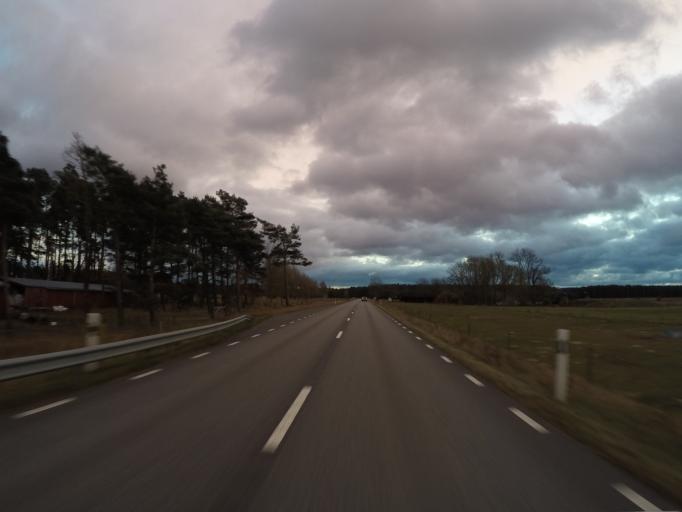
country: SE
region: Skane
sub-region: Kristianstads Kommun
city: Degeberga
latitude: 55.8844
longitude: 14.0872
